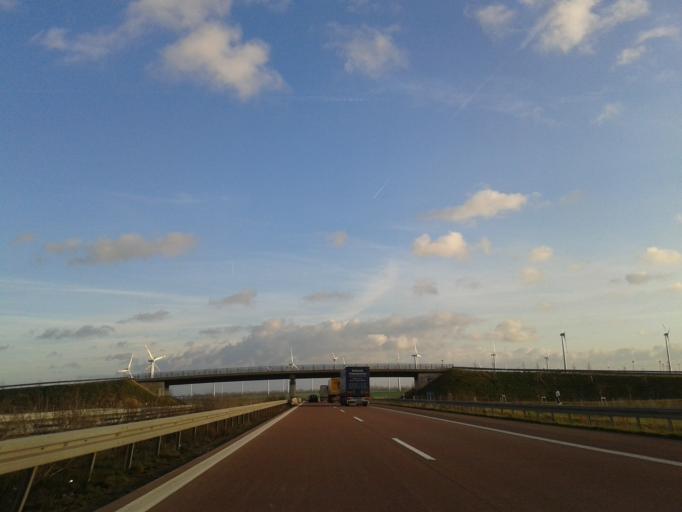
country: DE
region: Saxony-Anhalt
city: Obhausen
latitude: 51.4105
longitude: 11.6802
